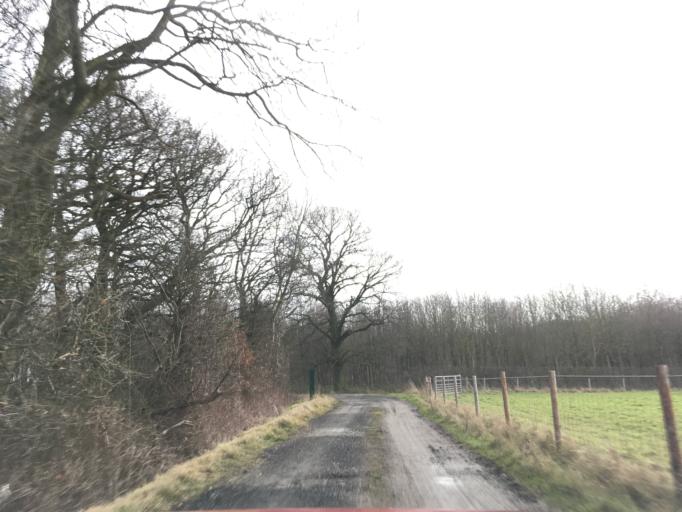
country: GB
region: England
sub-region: Nottinghamshire
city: Gotham
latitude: 52.8457
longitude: -1.1995
